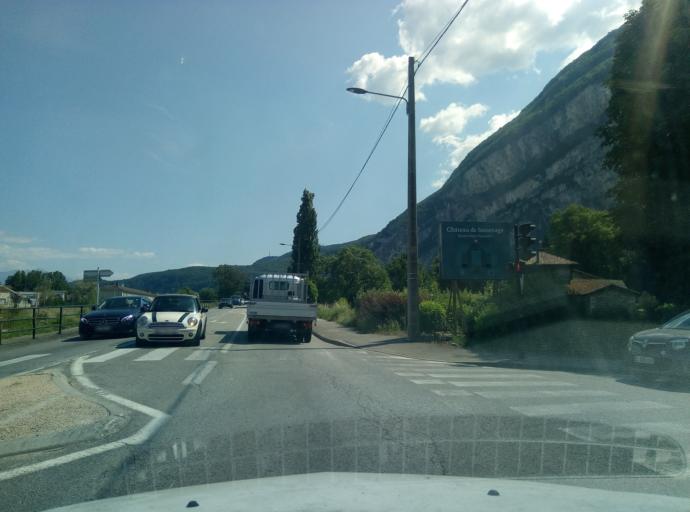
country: FR
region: Rhone-Alpes
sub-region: Departement de l'Isere
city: Sassenage
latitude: 45.2115
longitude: 5.6618
